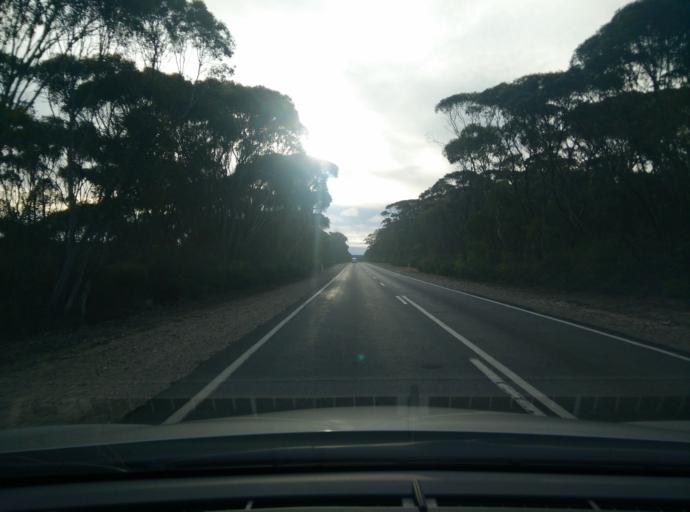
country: AU
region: South Australia
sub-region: Kangaroo Island
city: Kingscote
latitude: -35.7986
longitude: 137.8487
